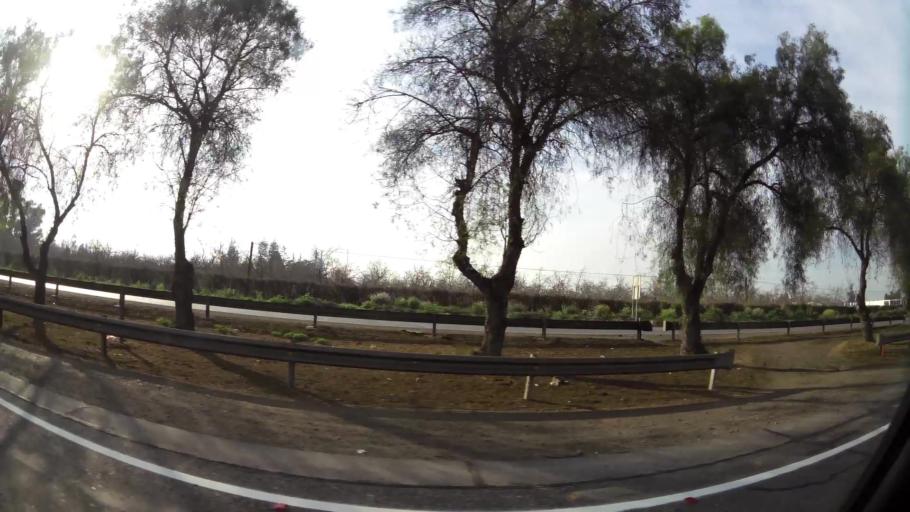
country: CL
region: Santiago Metropolitan
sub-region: Provincia de Talagante
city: Penaflor
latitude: -33.5932
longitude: -70.8425
